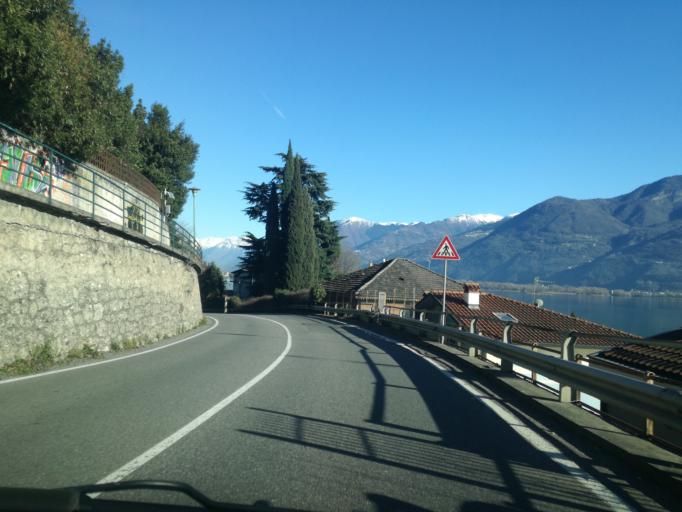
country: IT
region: Lombardy
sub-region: Provincia di Bergamo
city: Lovere
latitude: 45.8102
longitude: 10.0689
